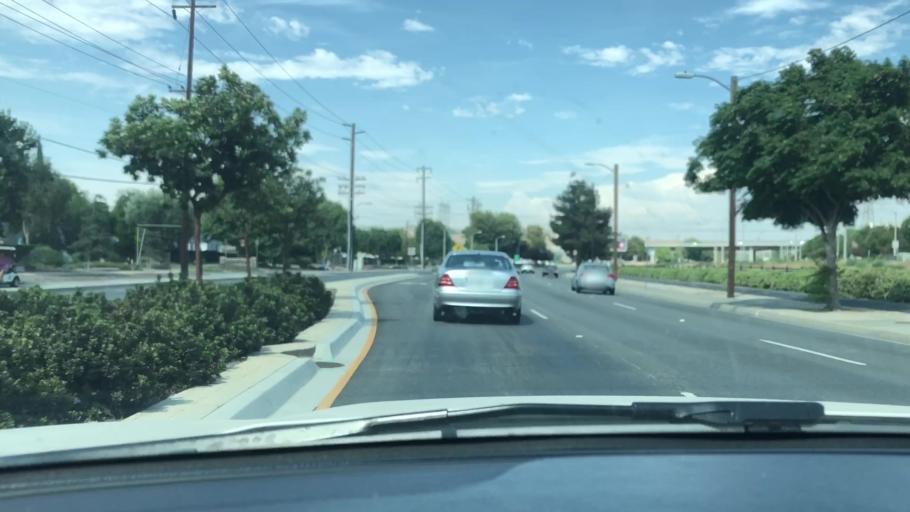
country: US
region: California
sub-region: Los Angeles County
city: Santa Clarita
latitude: 34.4188
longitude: -118.5080
